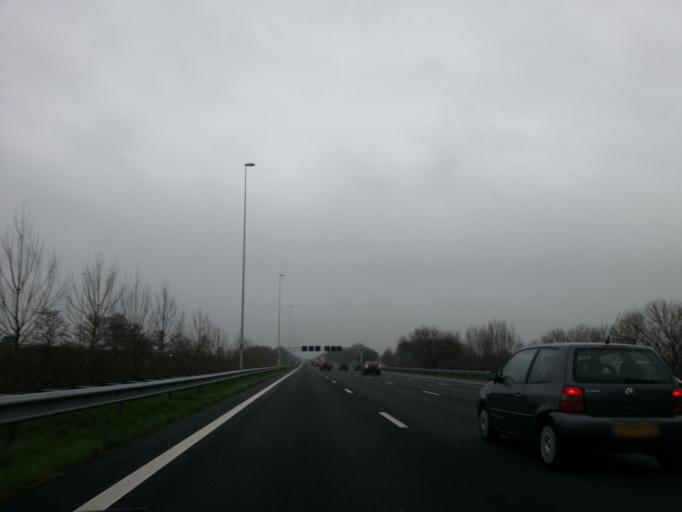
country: NL
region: Utrecht
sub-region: Gemeente Woerden
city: Woerden
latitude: 52.0695
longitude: 4.8483
